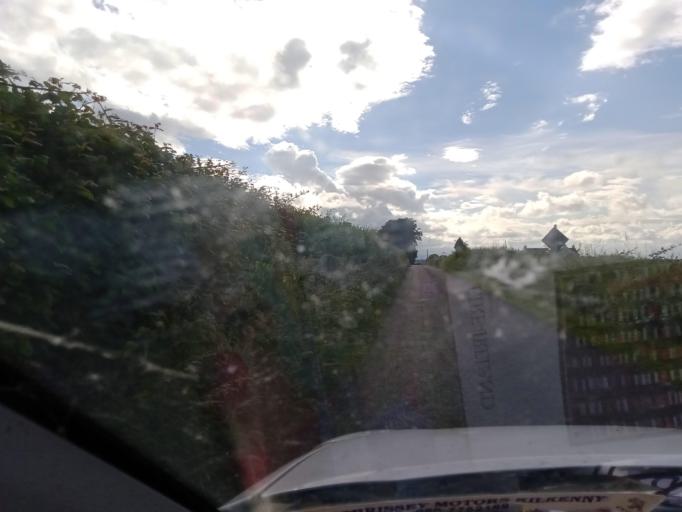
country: IE
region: Leinster
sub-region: Laois
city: Rathdowney
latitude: 52.7726
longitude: -7.5026
